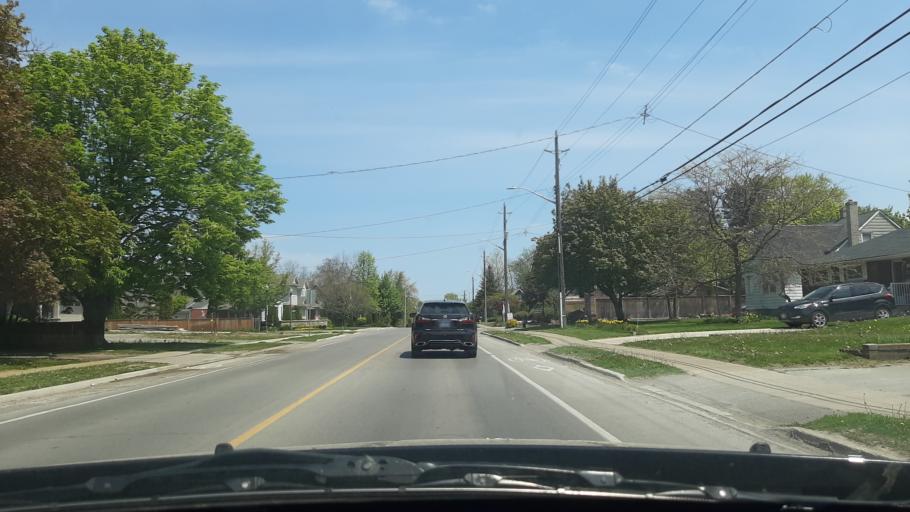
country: US
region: New York
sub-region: Niagara County
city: Youngstown
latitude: 43.2190
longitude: -79.1260
